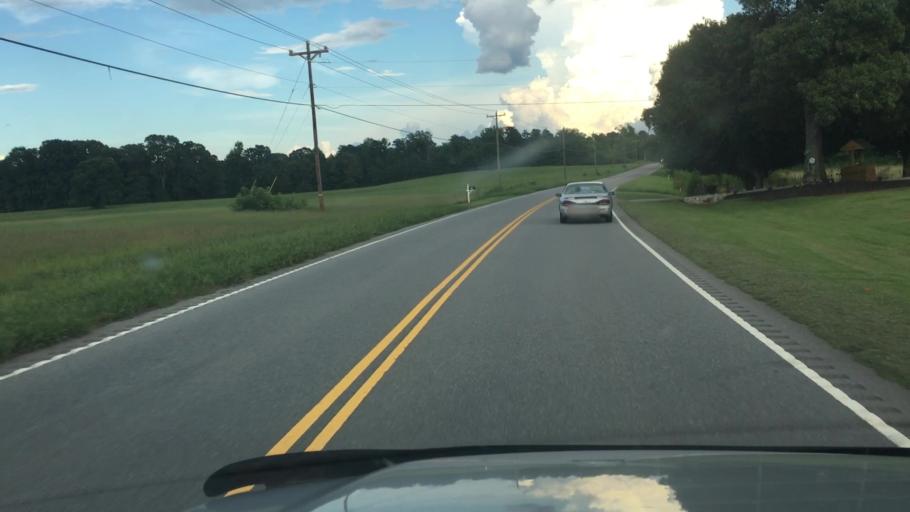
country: US
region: South Carolina
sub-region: Cherokee County
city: Gaffney
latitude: 35.1181
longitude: -81.7135
